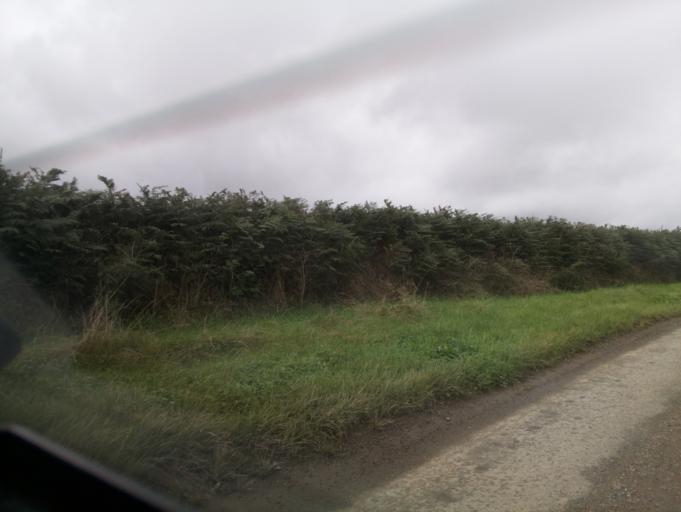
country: GB
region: England
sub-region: Devon
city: Dartmouth
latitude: 50.3423
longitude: -3.6370
